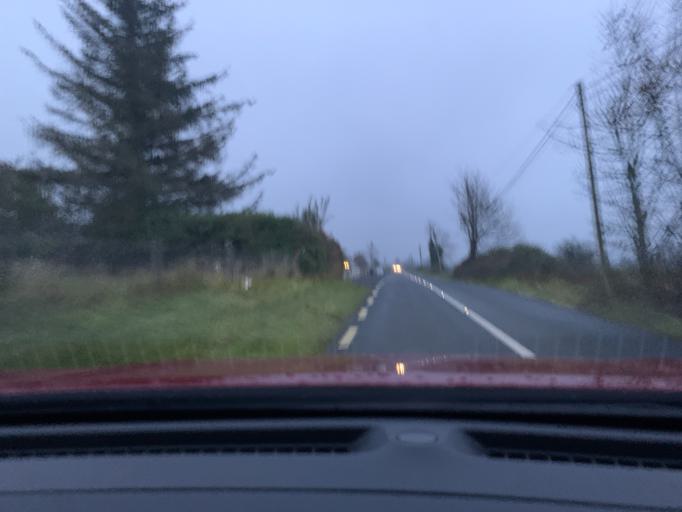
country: IE
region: Connaught
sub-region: Sligo
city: Ballymote
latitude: 54.0197
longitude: -8.5624
